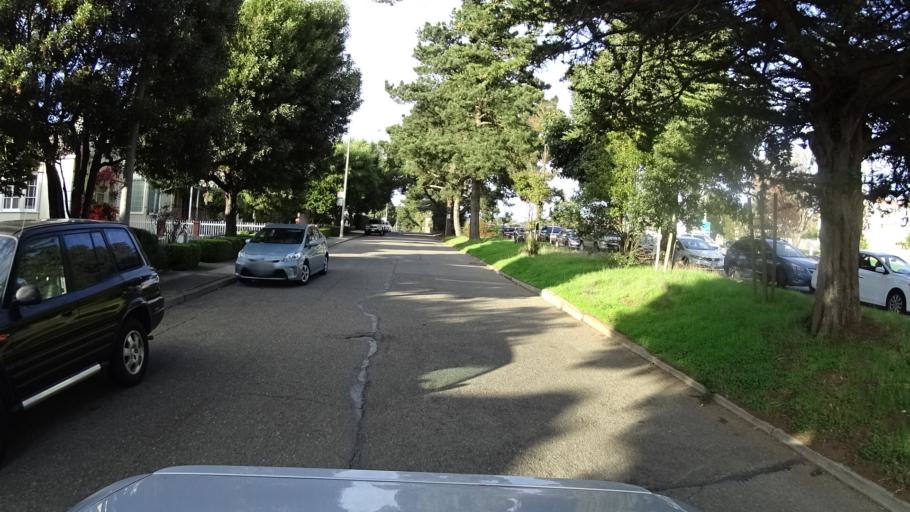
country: US
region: California
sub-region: San Mateo County
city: Daly City
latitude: 37.7259
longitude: -122.4725
